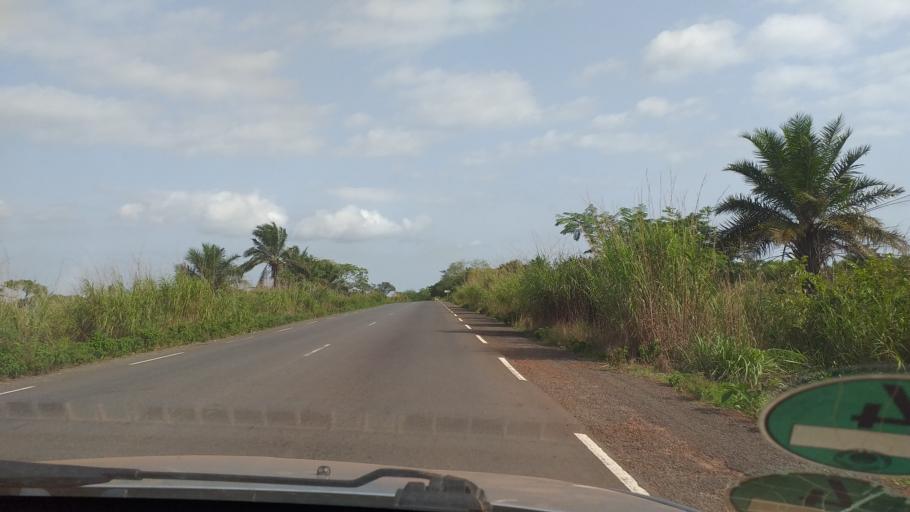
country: GN
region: Boke
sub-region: Boke Prefecture
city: Sangueya
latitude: 10.4397
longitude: -14.4029
